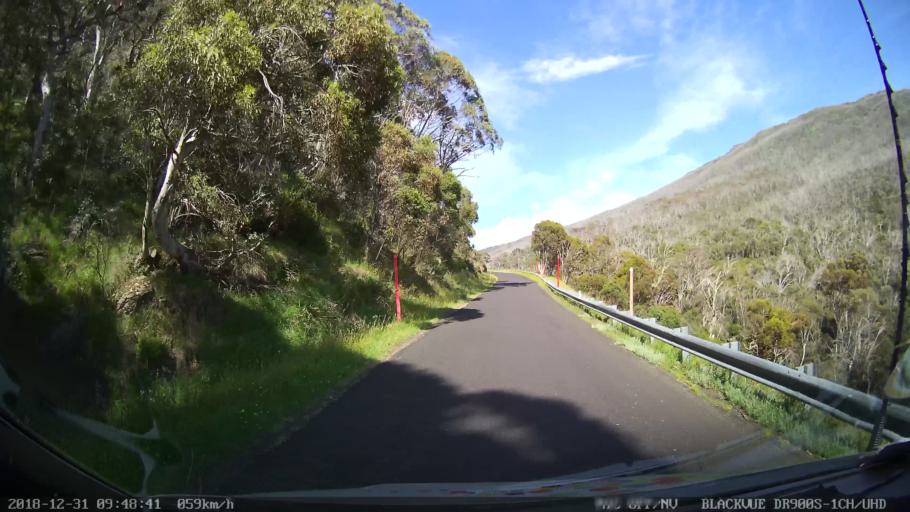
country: AU
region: New South Wales
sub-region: Snowy River
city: Jindabyne
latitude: -36.5139
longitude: 148.2900
